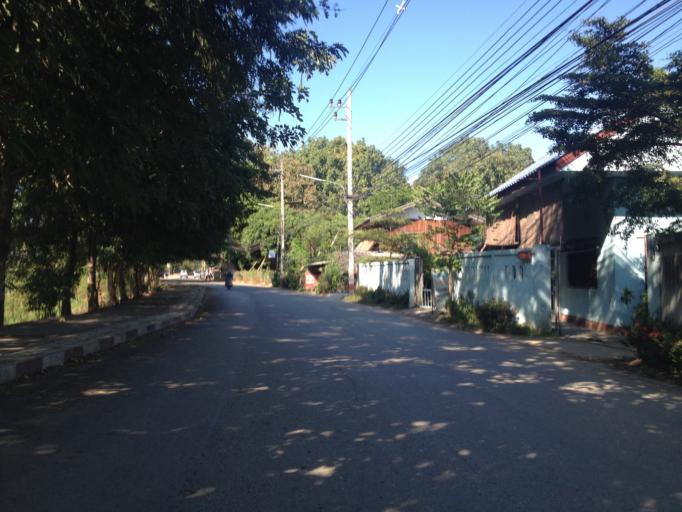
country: TH
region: Chiang Mai
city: Saraphi
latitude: 18.7177
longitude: 98.9877
